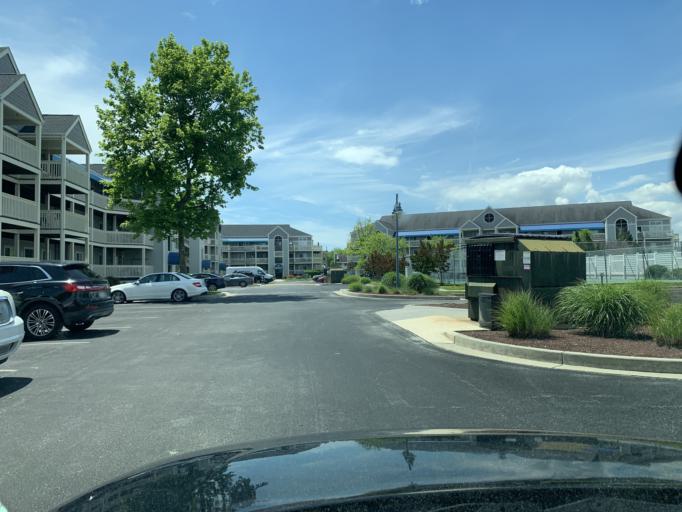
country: US
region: Maryland
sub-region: Worcester County
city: Ocean City
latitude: 38.4294
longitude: -75.0616
